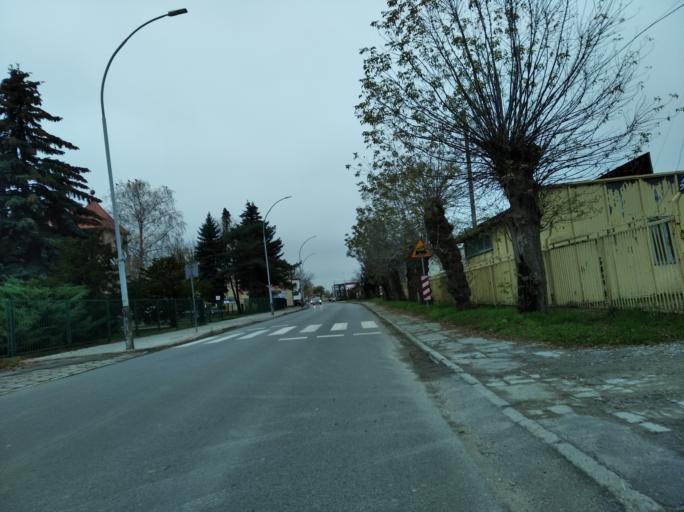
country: PL
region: Subcarpathian Voivodeship
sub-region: Krosno
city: Krosno
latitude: 49.6924
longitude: 21.7522
